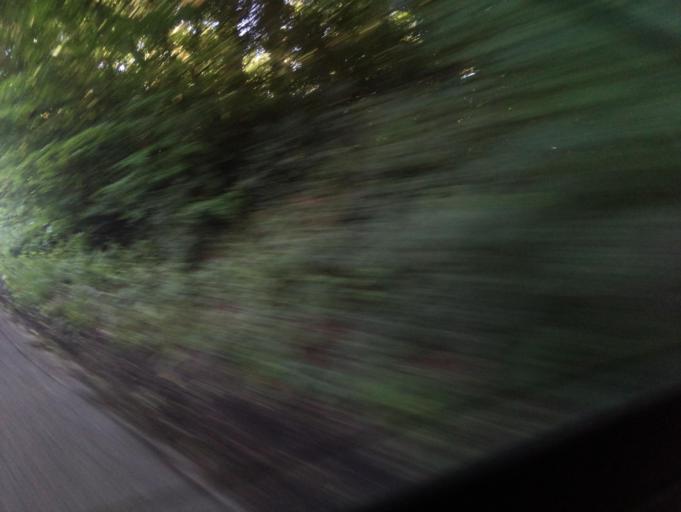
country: GB
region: England
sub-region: Devon
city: Topsham
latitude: 50.7155
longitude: -3.3890
